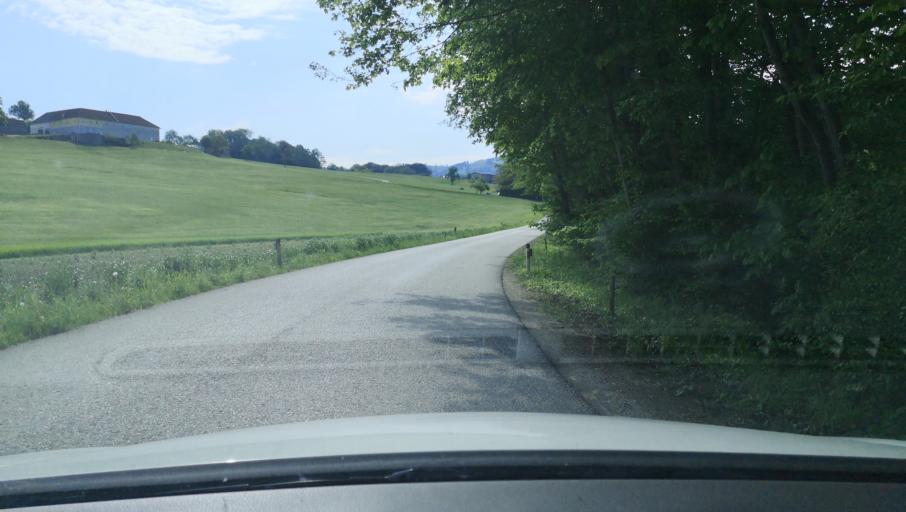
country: AT
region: Lower Austria
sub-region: Politischer Bezirk Amstetten
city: Neuhofen an der Ybbs
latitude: 48.0518
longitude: 14.8807
